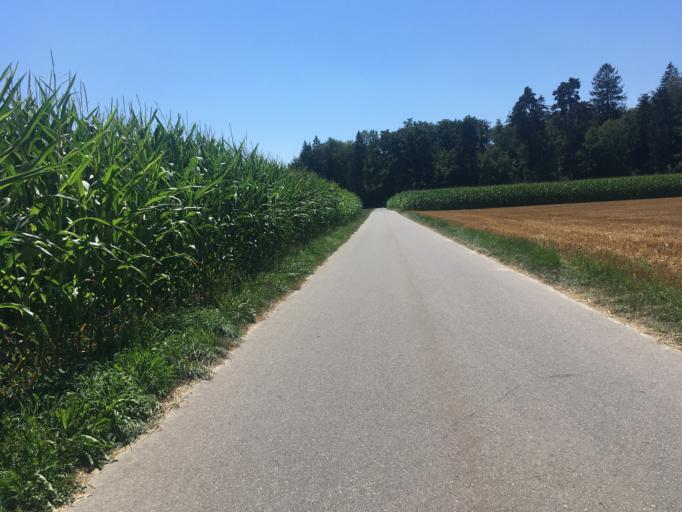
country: CH
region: Solothurn
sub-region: Bezirk Bucheggberg
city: Messen
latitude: 47.0816
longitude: 7.4616
